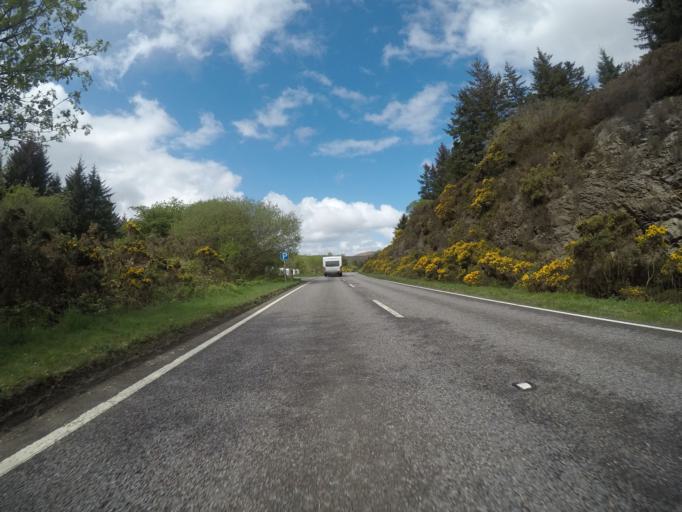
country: GB
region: Scotland
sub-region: Highland
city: Portree
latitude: 57.2453
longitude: -5.9248
